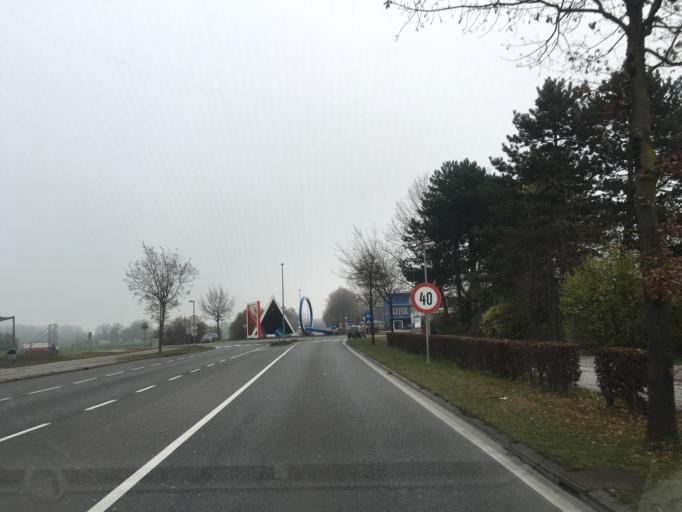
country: AT
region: Vorarlberg
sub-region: Politischer Bezirk Dornbirn
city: Lustenau
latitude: 47.4177
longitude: 9.6710
